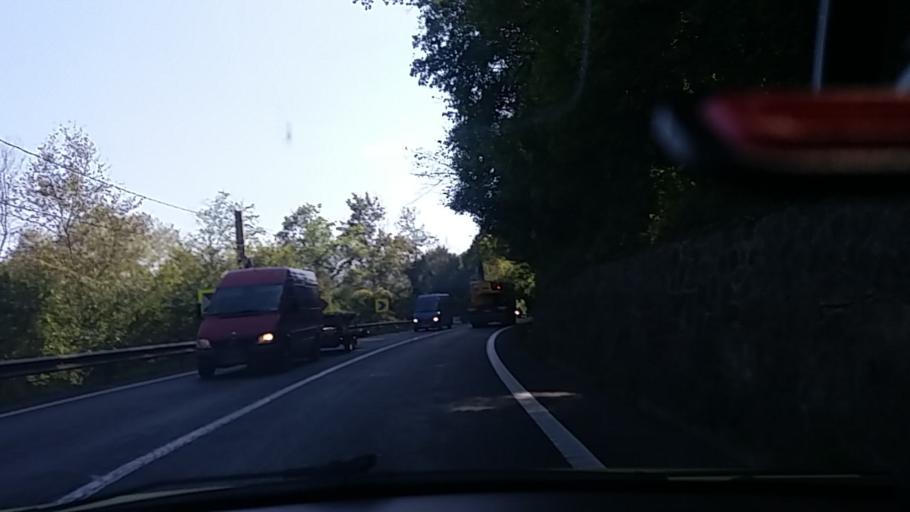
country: RO
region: Hunedoara
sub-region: Comuna Branisca
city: Branisca
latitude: 45.9078
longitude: 22.7745
